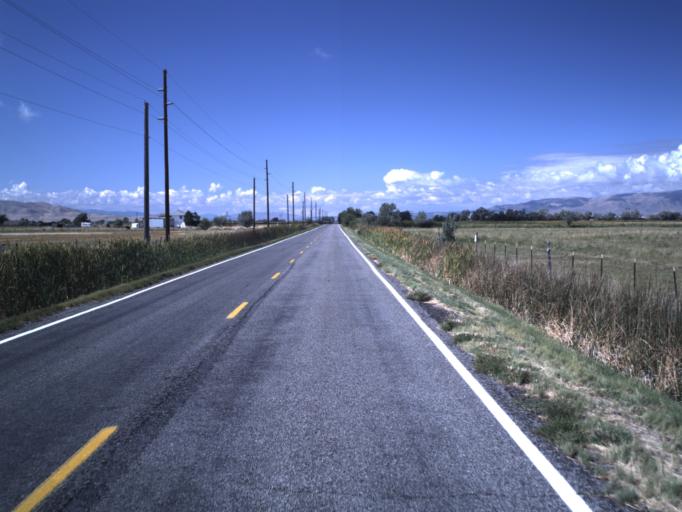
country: US
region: Utah
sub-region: Utah County
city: Spanish Fork
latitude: 40.1586
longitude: -111.6663
